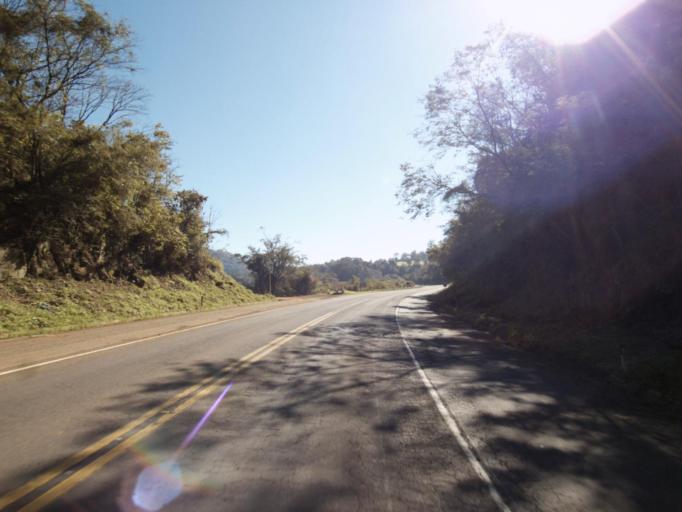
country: BR
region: Rio Grande do Sul
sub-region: Frederico Westphalen
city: Frederico Westphalen
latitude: -27.0029
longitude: -53.2260
